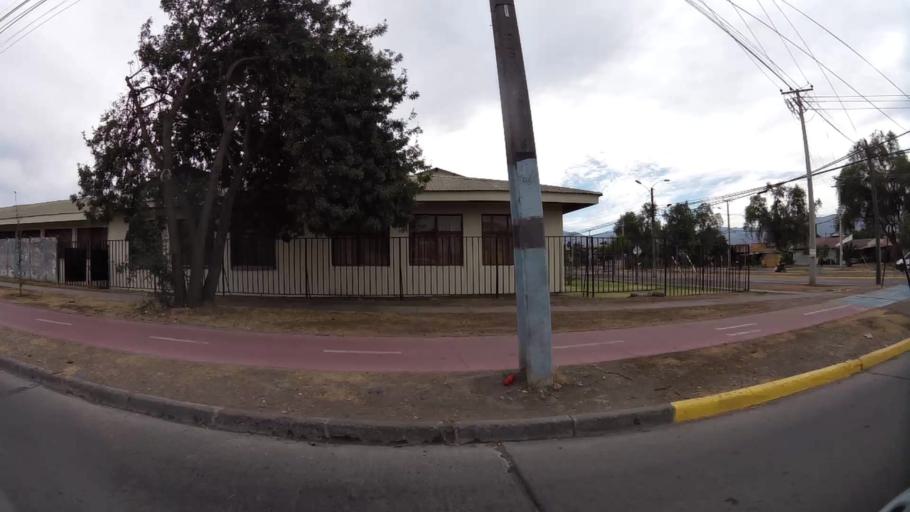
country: CL
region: O'Higgins
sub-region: Provincia de Cachapoal
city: Rancagua
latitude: -34.1466
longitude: -70.7360
